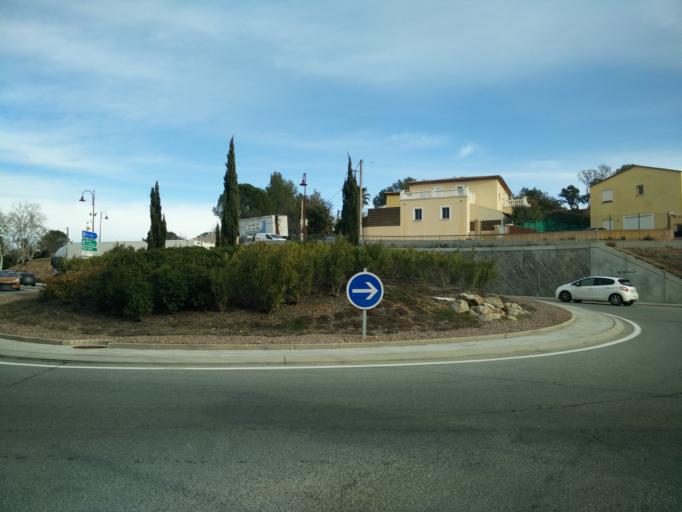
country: FR
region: Provence-Alpes-Cote d'Azur
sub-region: Departement du Var
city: Vidauban
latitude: 43.4311
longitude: 6.4364
